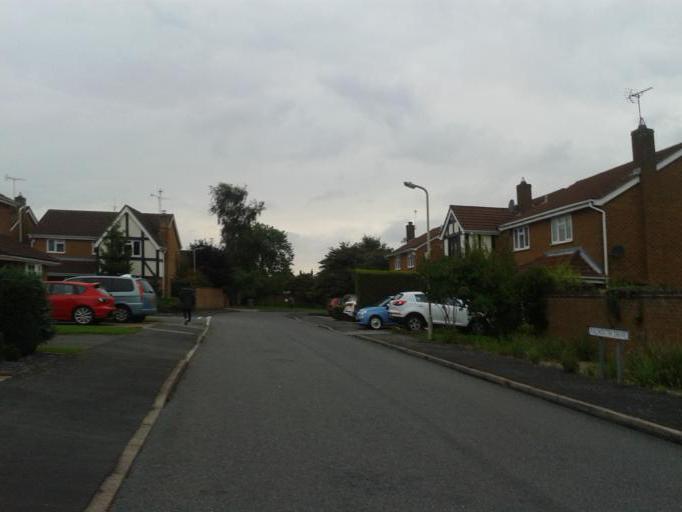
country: GB
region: England
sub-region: Leicestershire
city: Hinckley
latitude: 52.5576
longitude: -1.3633
